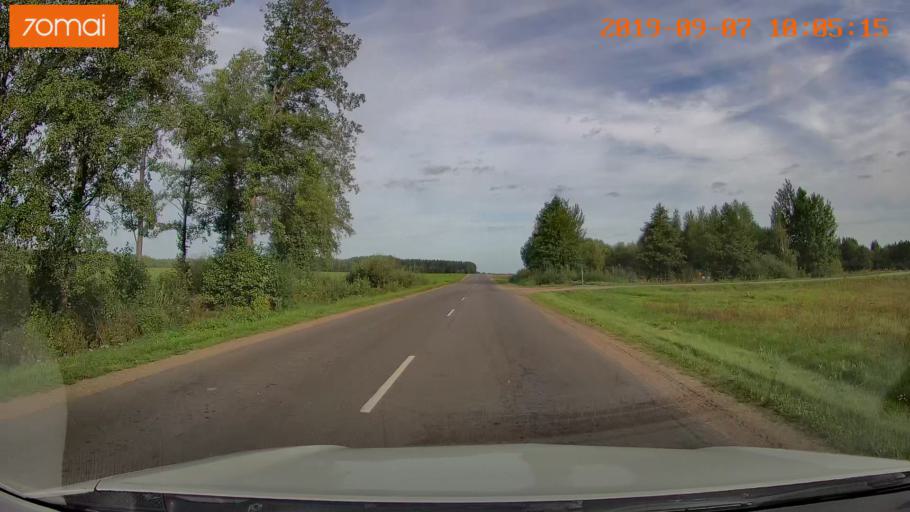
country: BY
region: Grodnenskaya
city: Voranava
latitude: 54.0448
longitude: 25.4084
